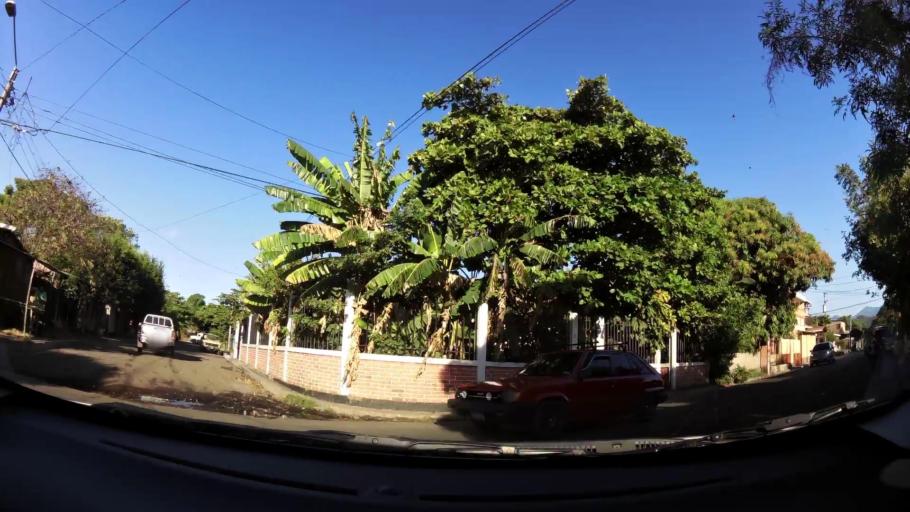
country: SV
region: Sonsonate
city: San Antonio del Monte
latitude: 13.7135
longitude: -89.7335
